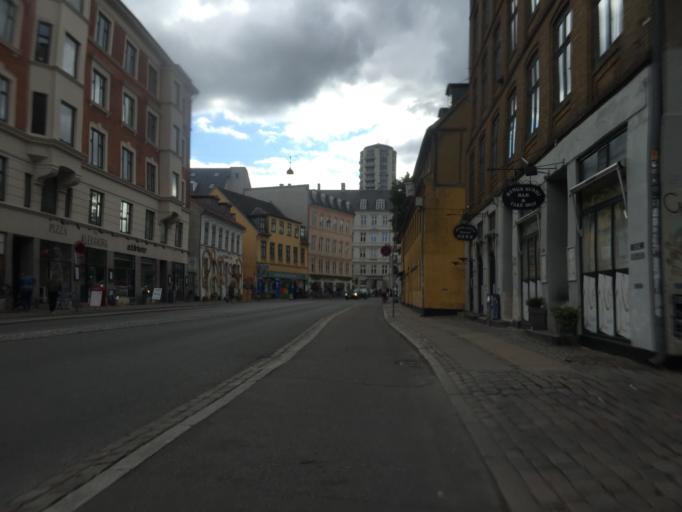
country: DK
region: Capital Region
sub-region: Frederiksberg Kommune
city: Frederiksberg
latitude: 55.6705
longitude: 12.5410
